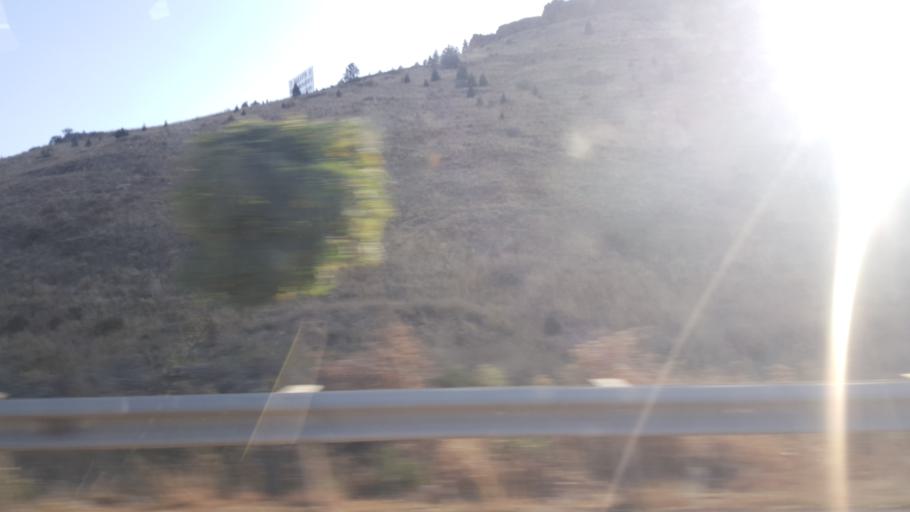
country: TR
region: Ankara
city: Polatli
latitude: 39.5780
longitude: 32.0623
